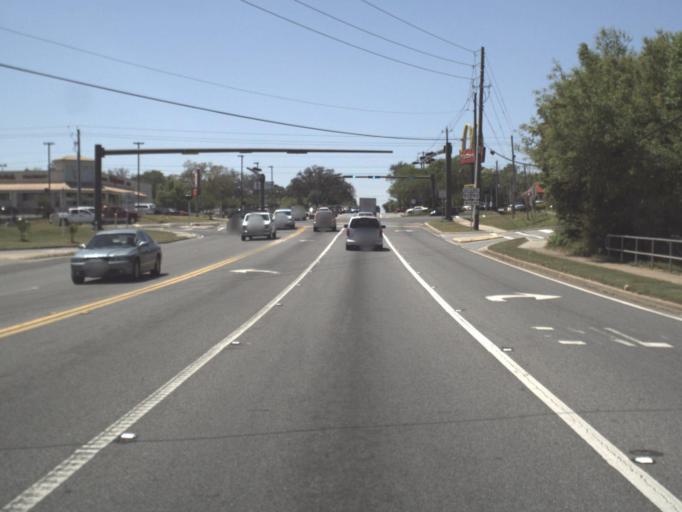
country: US
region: Florida
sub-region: Escambia County
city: Bellview
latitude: 30.4611
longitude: -87.2998
